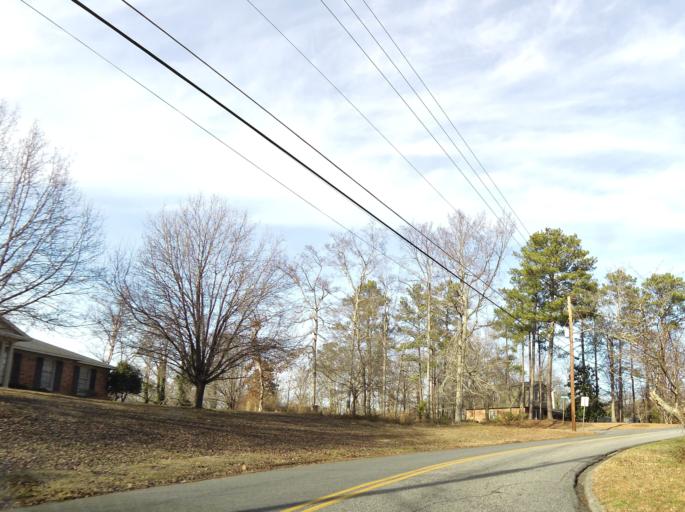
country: US
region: Georgia
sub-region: Bibb County
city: Macon
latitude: 32.8813
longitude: -83.7038
